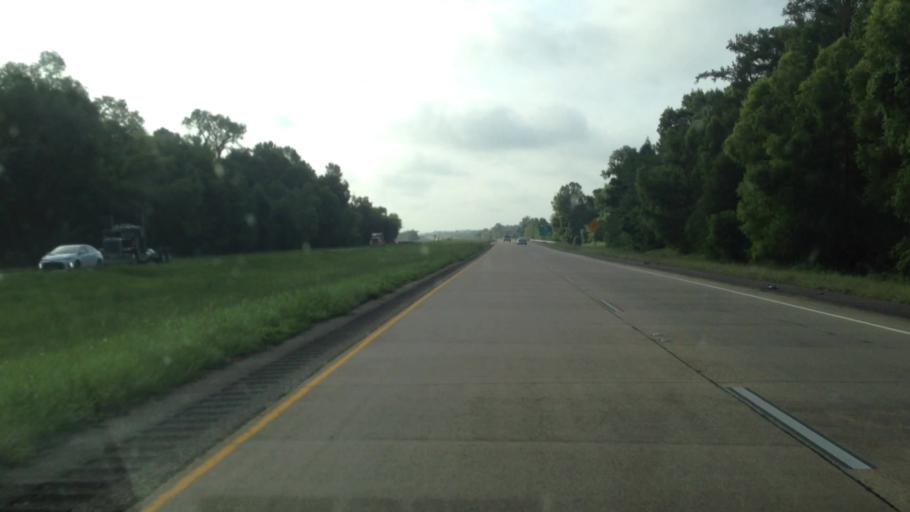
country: US
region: Louisiana
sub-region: Rapides Parish
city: Lecompte
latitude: 31.0214
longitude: -92.3921
